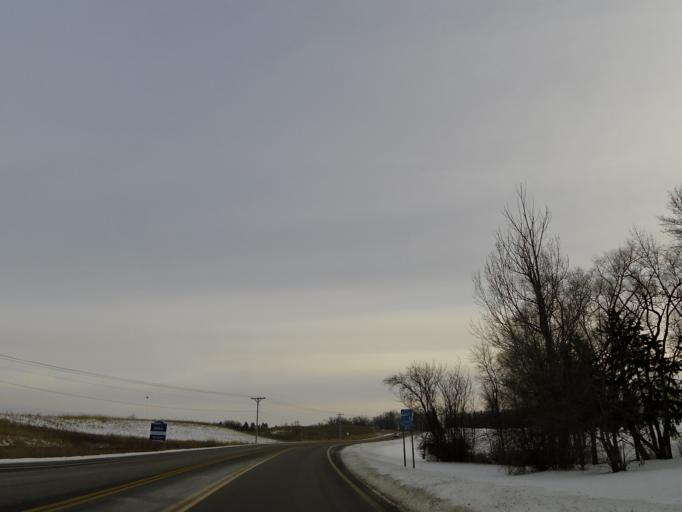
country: US
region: Minnesota
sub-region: Carver County
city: Victoria
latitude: 44.8483
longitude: -93.6560
